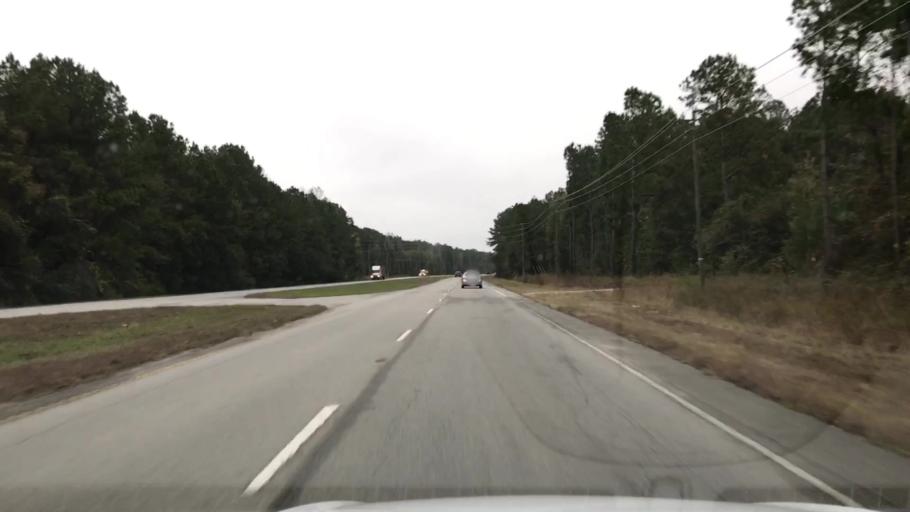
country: US
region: South Carolina
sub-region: Charleston County
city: Awendaw
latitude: 32.9524
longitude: -79.6953
